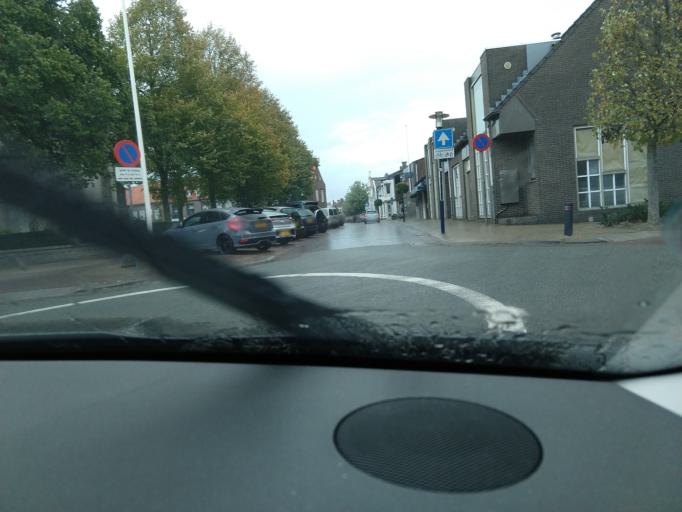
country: NL
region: Zeeland
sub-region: Gemeente Reimerswaal
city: Yerseke
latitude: 51.4919
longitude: 4.0489
